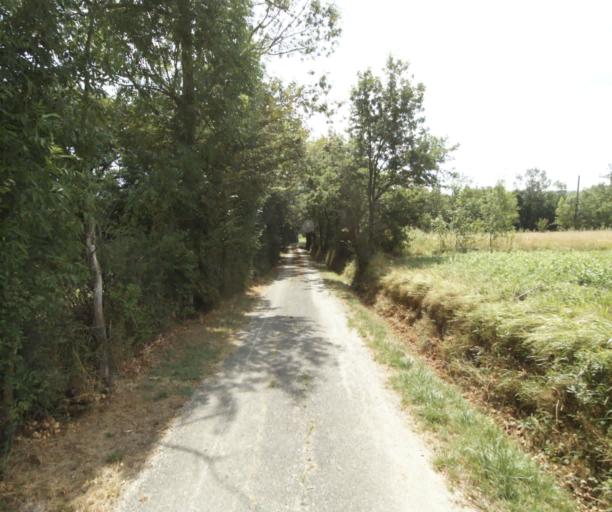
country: FR
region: Midi-Pyrenees
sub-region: Departement du Tarn
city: Soreze
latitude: 43.4754
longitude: 2.0766
